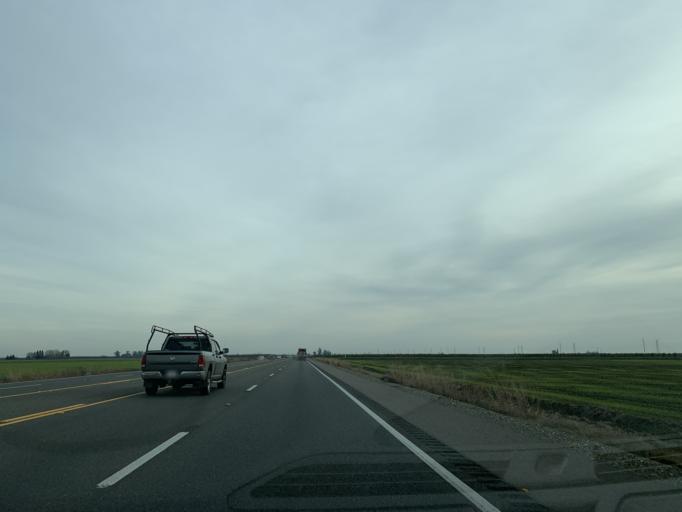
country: US
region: California
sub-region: Yuba County
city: Plumas Lake
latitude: 38.8799
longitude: -121.5659
